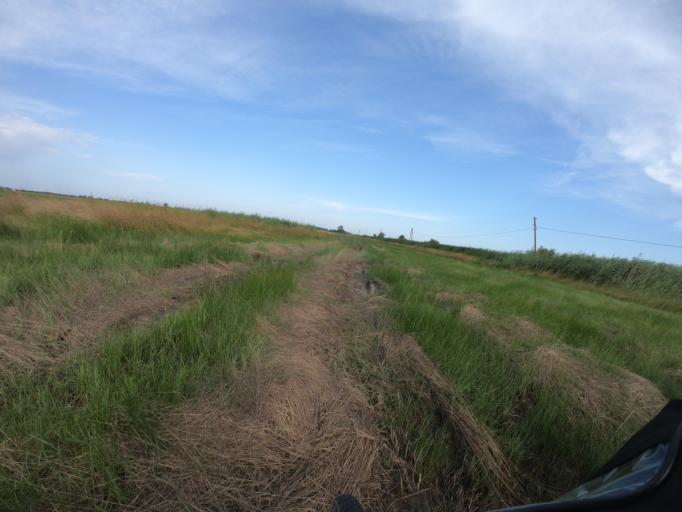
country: HU
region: Hajdu-Bihar
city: Tiszacsege
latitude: 47.6119
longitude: 21.0328
